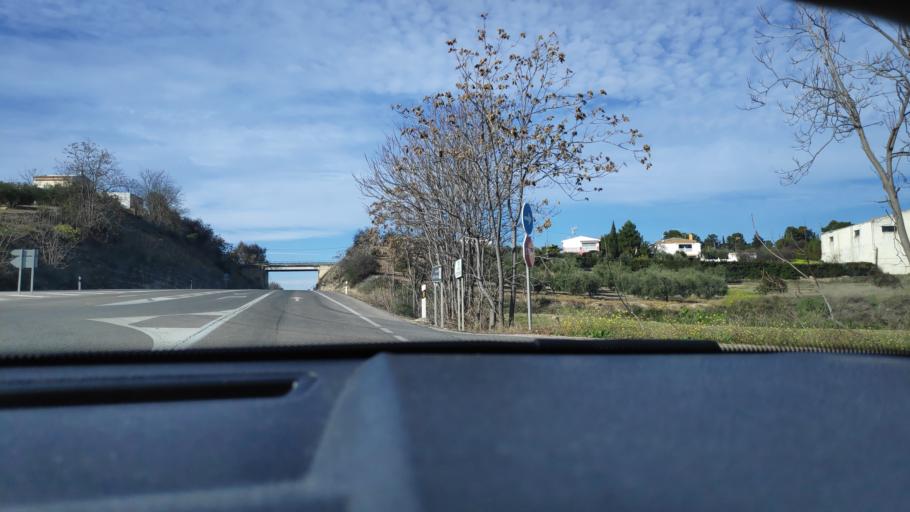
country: ES
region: Andalusia
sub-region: Provincia de Jaen
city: Porcuna
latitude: 37.8716
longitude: -4.1696
